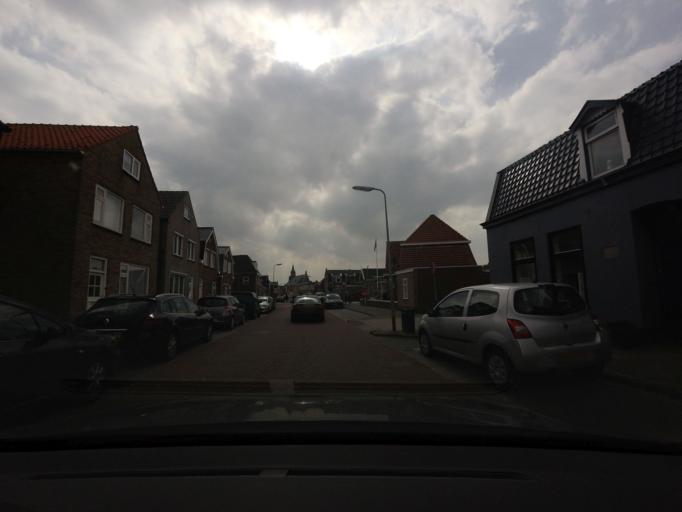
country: NL
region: North Holland
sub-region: Gemeente Bergen
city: Egmond aan Zee
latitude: 52.6210
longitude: 4.6247
